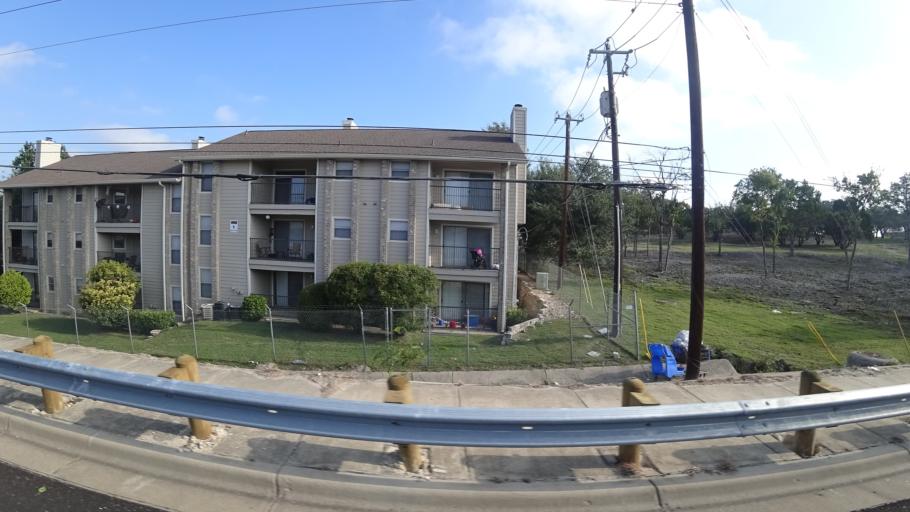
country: US
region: Texas
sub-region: Travis County
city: Austin
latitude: 30.3292
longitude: -97.6782
